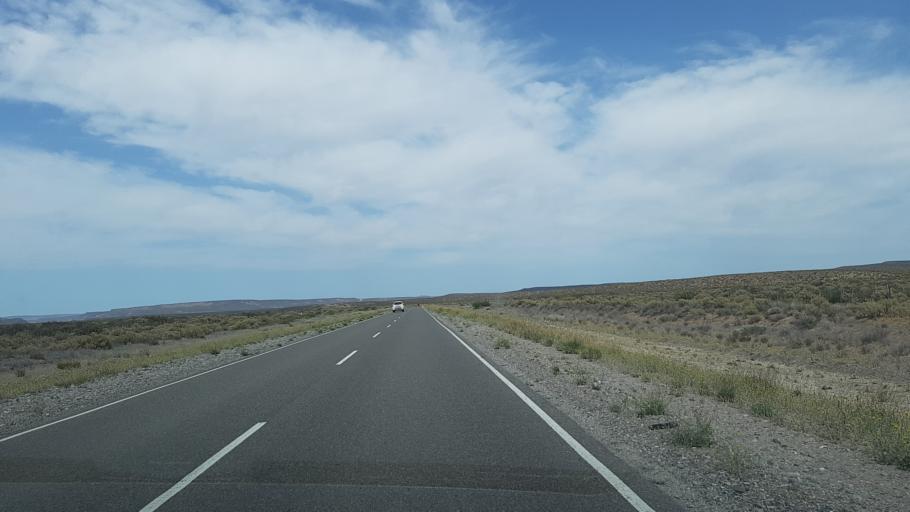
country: AR
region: Neuquen
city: Piedra del Aguila
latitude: -39.9011
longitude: -69.9023
